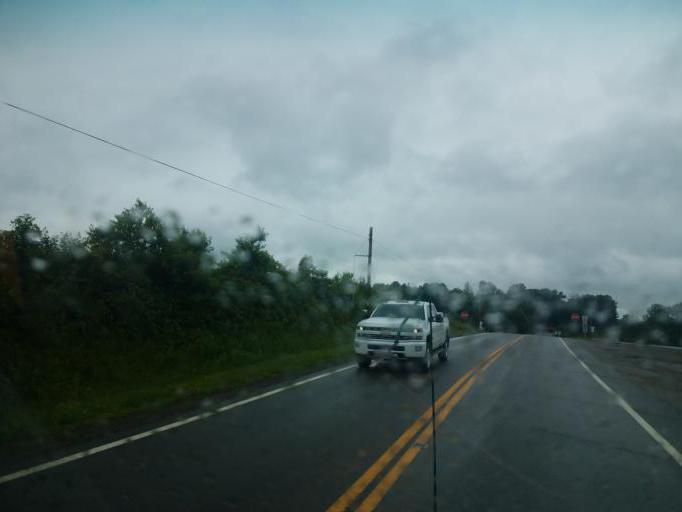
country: US
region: Ohio
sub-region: Carroll County
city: Carrollton
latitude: 40.5211
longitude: -81.0277
